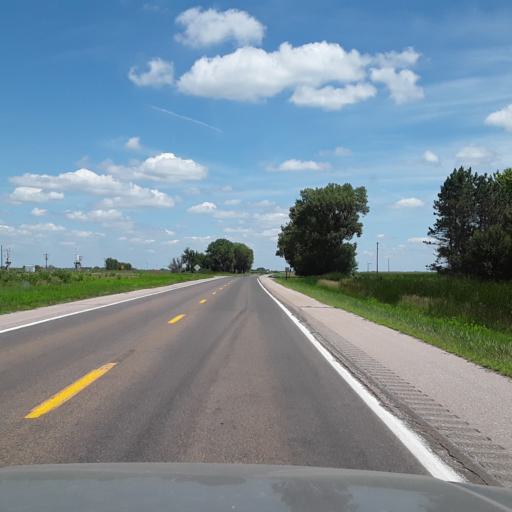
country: US
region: Nebraska
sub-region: Merrick County
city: Central City
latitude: 41.2181
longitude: -97.8305
